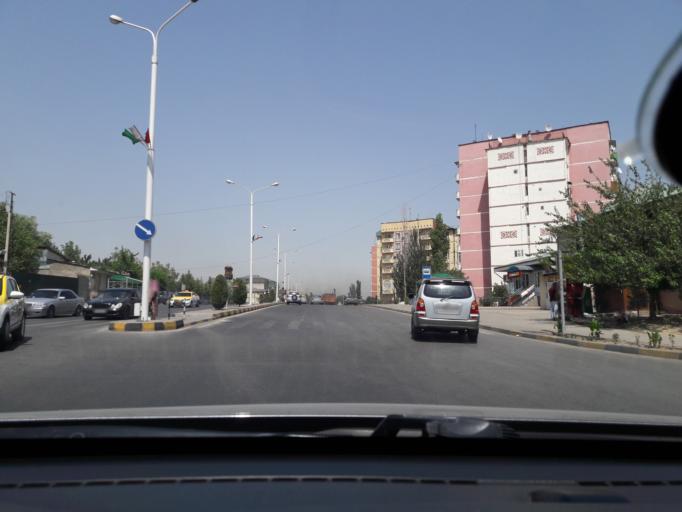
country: TJ
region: Dushanbe
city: Dushanbe
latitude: 38.5866
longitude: 68.7144
